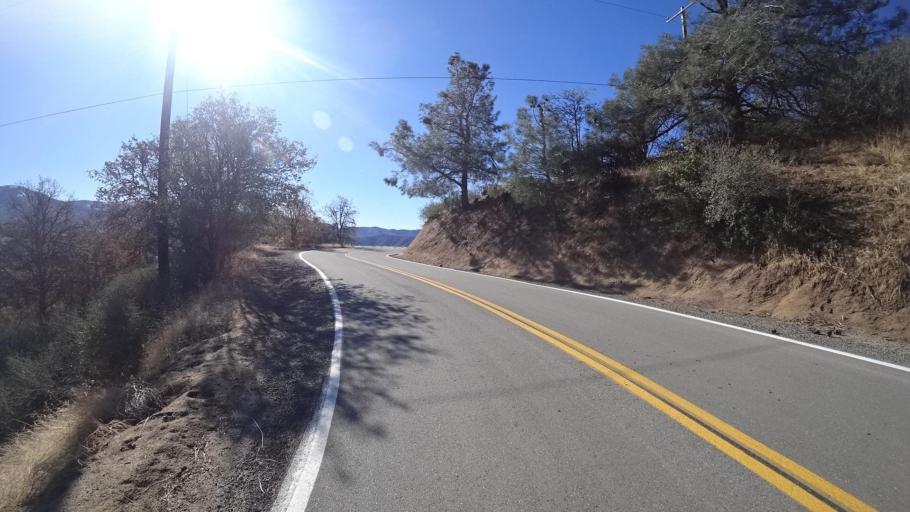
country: US
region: California
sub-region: Kern County
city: Alta Sierra
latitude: 35.7389
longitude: -118.6263
